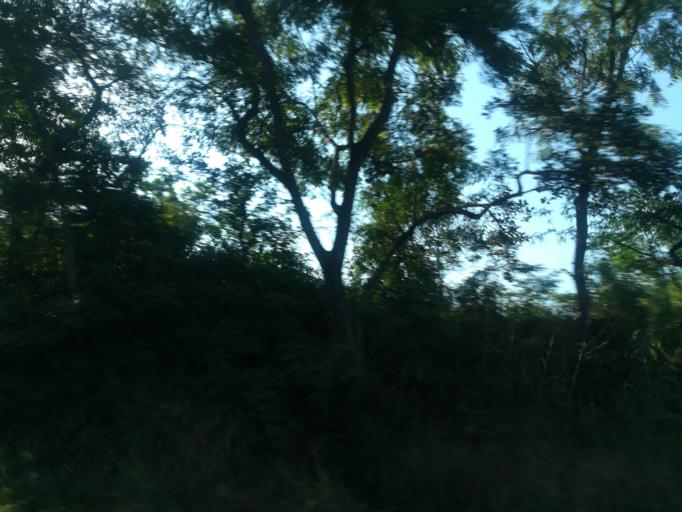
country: NG
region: Ogun
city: Abeokuta
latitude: 7.2244
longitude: 3.2996
